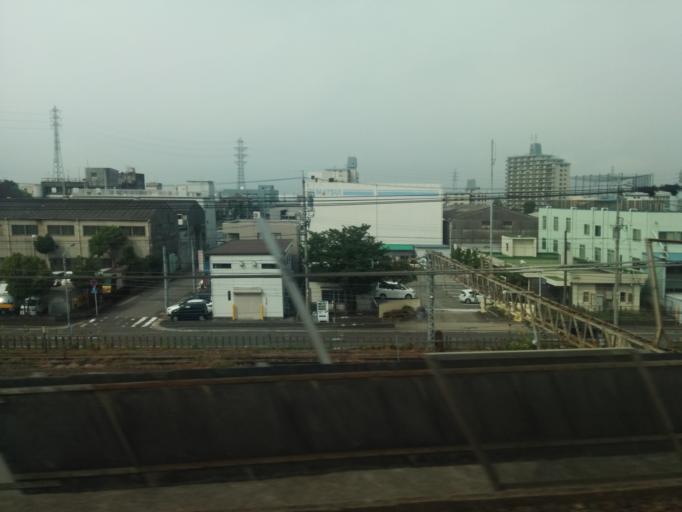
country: JP
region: Aichi
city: Nagoya-shi
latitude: 35.0989
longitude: 136.9246
